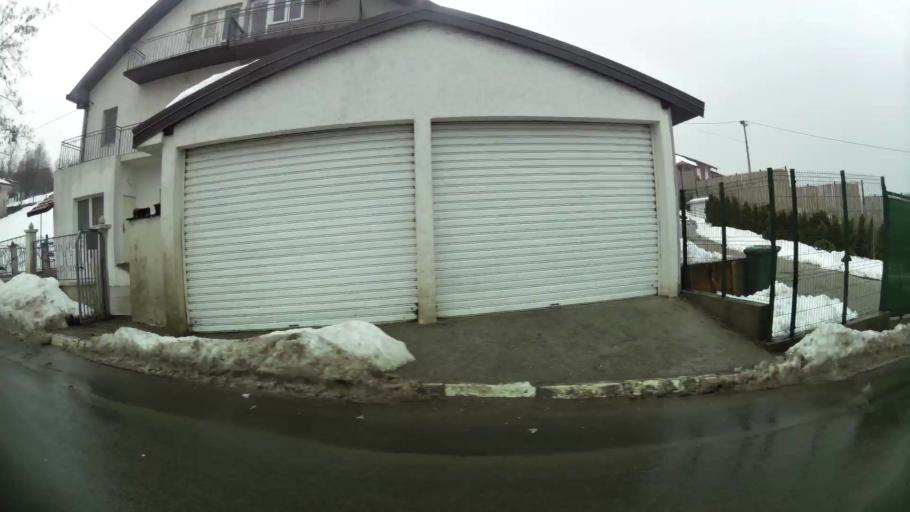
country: RS
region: Central Serbia
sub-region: Belgrade
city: Zvezdara
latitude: 44.7624
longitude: 20.5258
